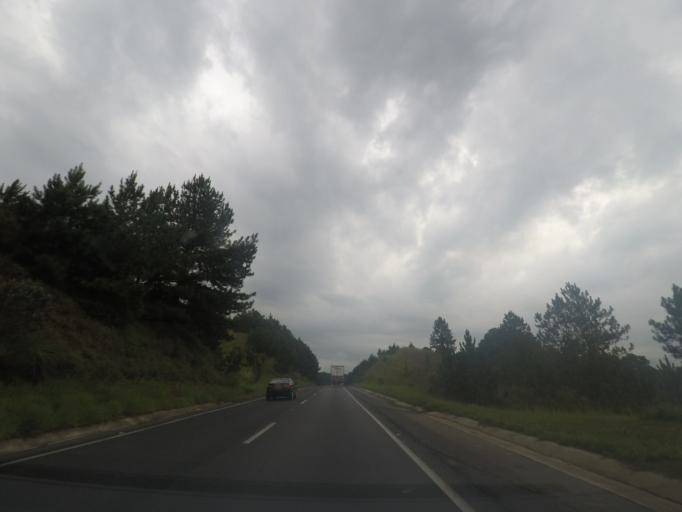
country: BR
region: Parana
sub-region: Campina Grande Do Sul
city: Campina Grande do Sul
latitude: -25.1081
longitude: -48.8508
